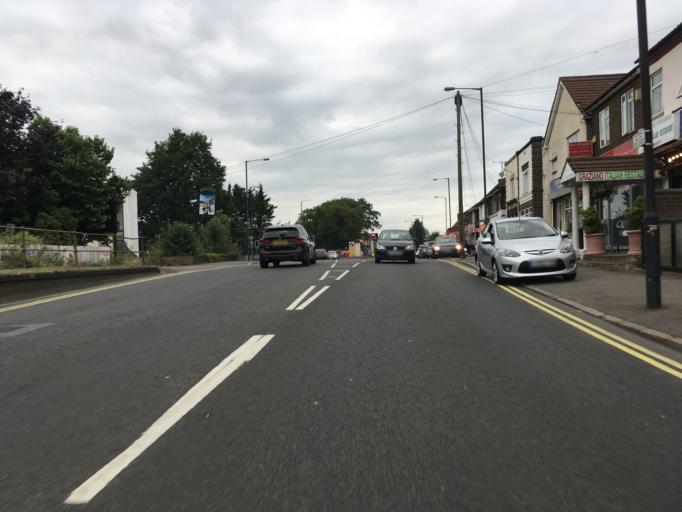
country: GB
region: England
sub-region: Central Bedfordshire
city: Dunstable
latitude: 51.8935
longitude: -0.5313
